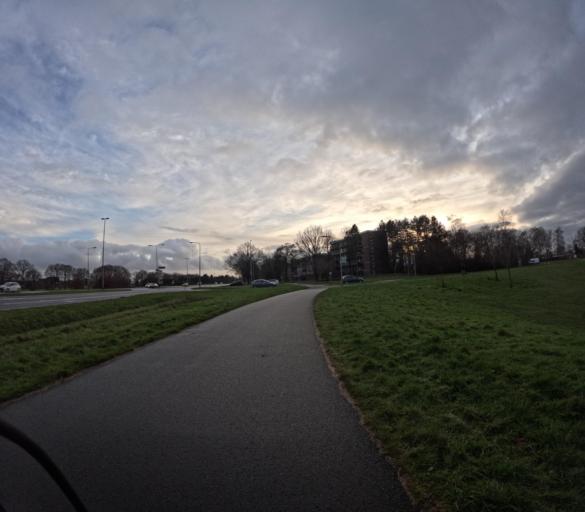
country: NL
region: Drenthe
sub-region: Gemeente Emmen
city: Emmen
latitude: 52.7922
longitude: 6.9496
